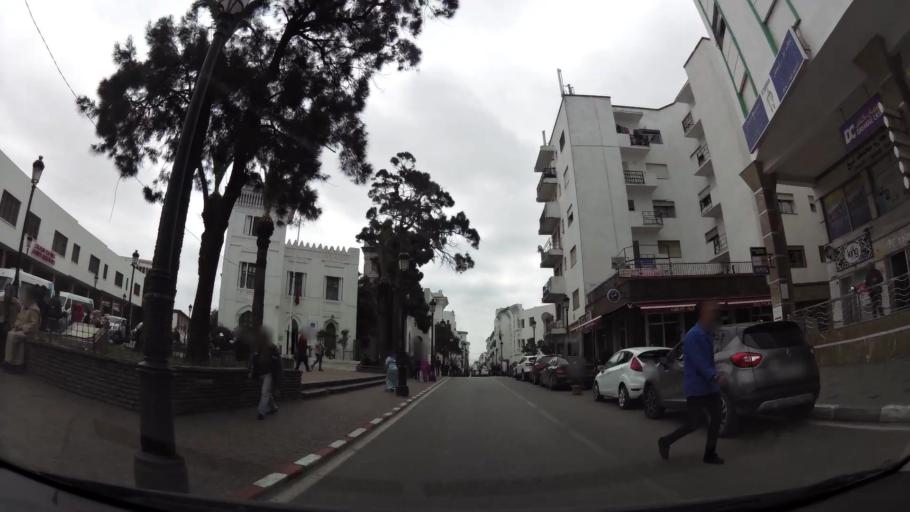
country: MA
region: Tanger-Tetouan
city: Tetouan
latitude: 35.5727
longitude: -5.3781
